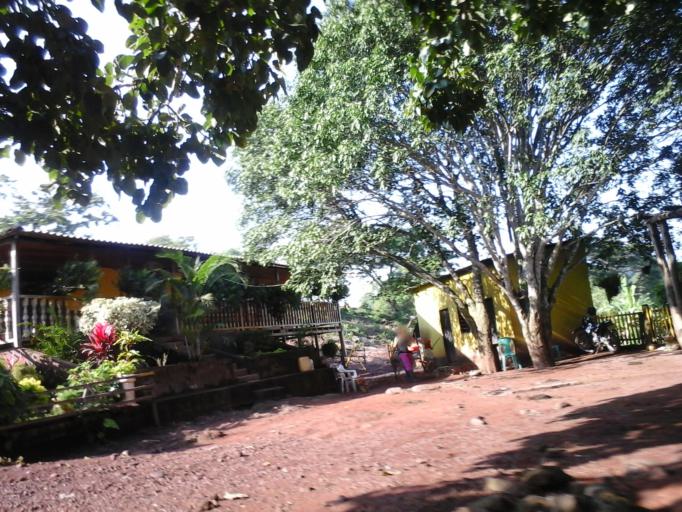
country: CO
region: Cesar
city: Agustin Codazzi
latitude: 10.0311
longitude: -73.2337
